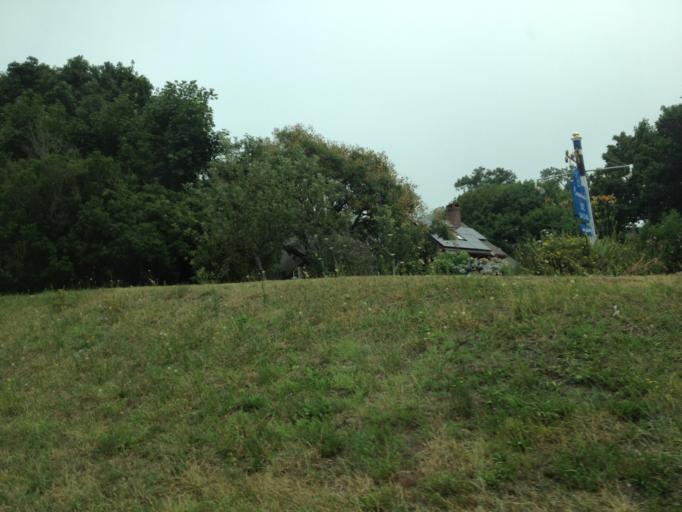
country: US
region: Massachusetts
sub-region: Barnstable County
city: Eastham
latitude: 41.8182
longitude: -69.9687
